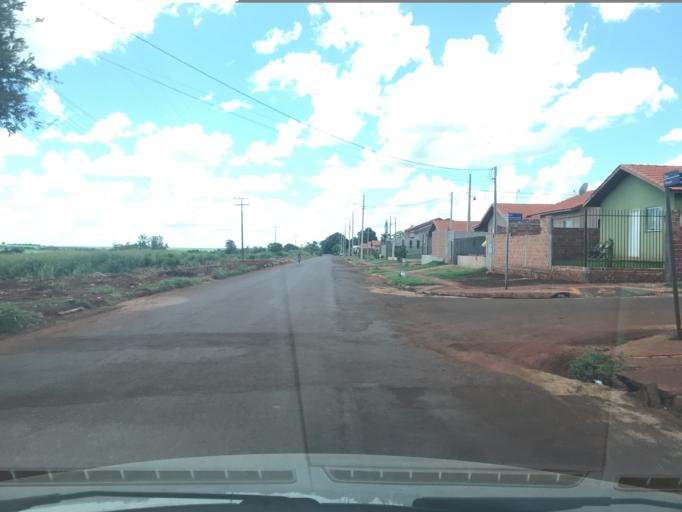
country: BR
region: Parana
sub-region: Palotina
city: Palotina
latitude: -24.2672
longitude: -53.8485
